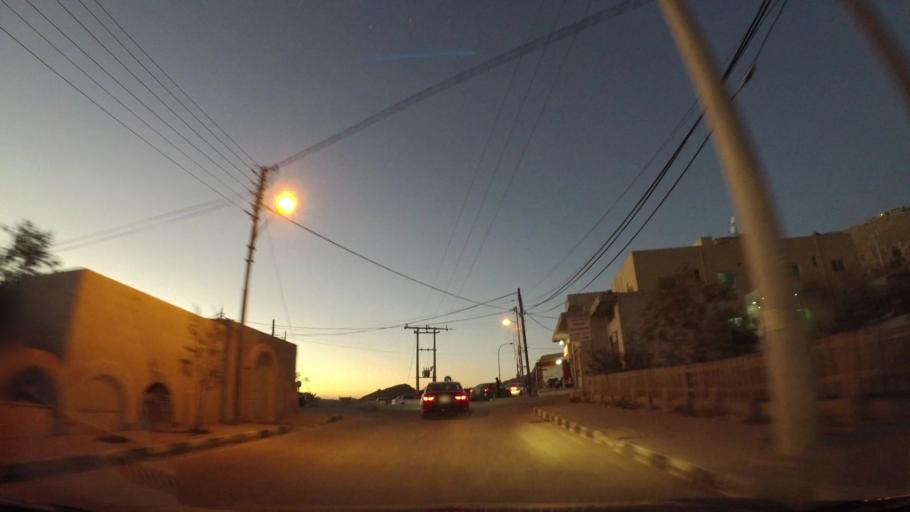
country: JO
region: Ma'an
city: Petra
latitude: 30.3281
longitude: 35.4703
